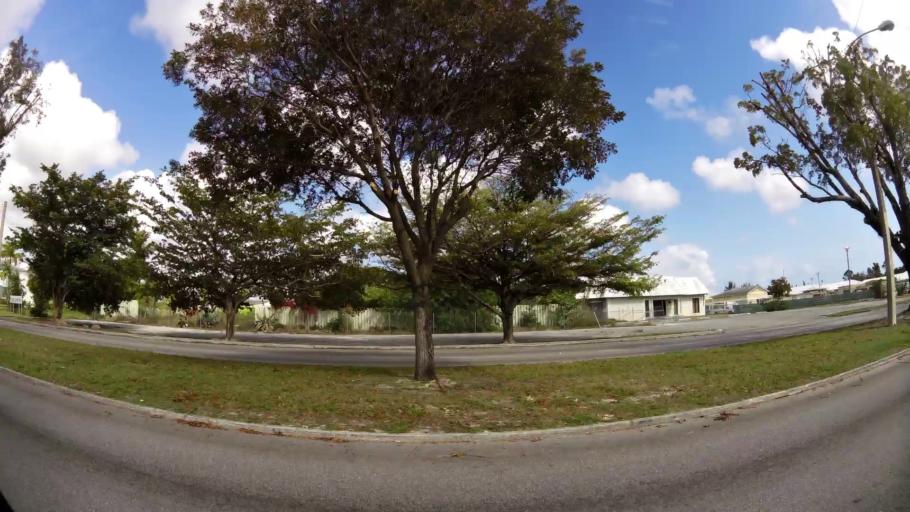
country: BS
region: Freeport
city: Freeport
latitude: 26.5338
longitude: -78.6935
